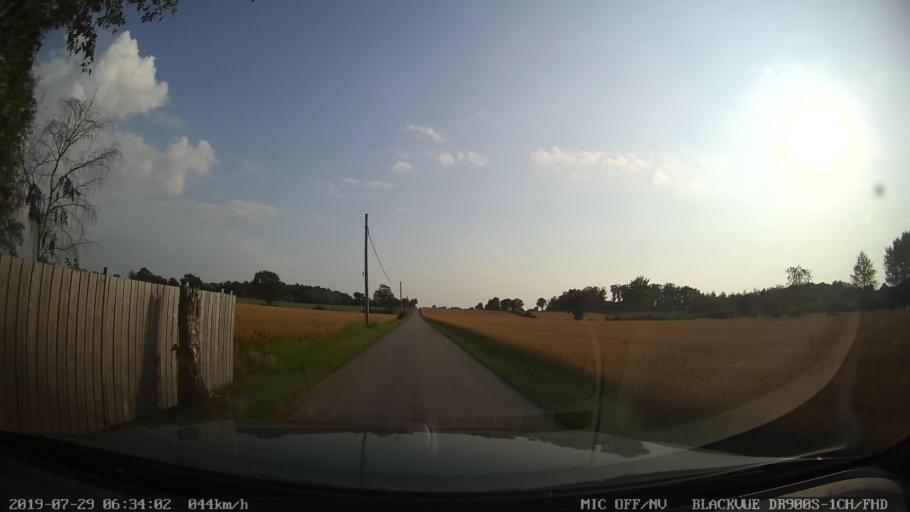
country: SE
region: Skane
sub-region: Helsingborg
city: Odakra
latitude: 56.1226
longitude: 12.7288
